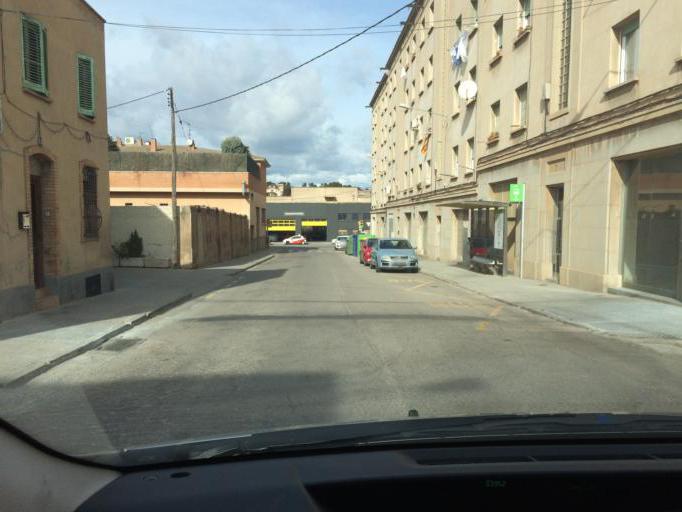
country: ES
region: Catalonia
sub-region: Provincia de Barcelona
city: Manresa
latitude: 41.7329
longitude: 1.8398
